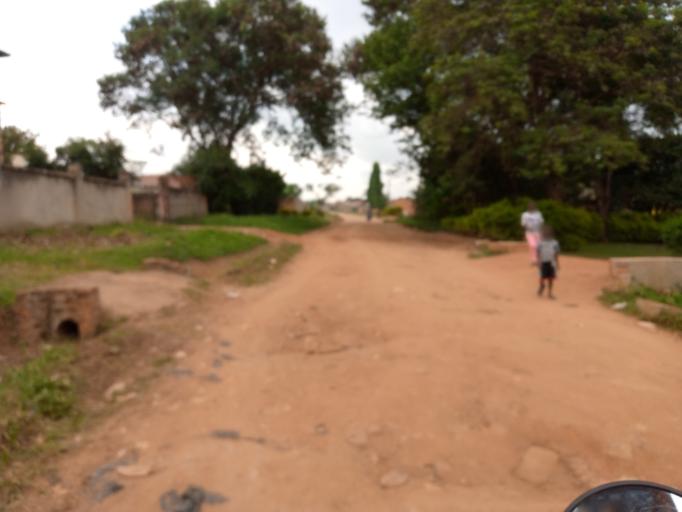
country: UG
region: Eastern Region
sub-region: Mbale District
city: Mbale
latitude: 1.0862
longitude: 34.1723
